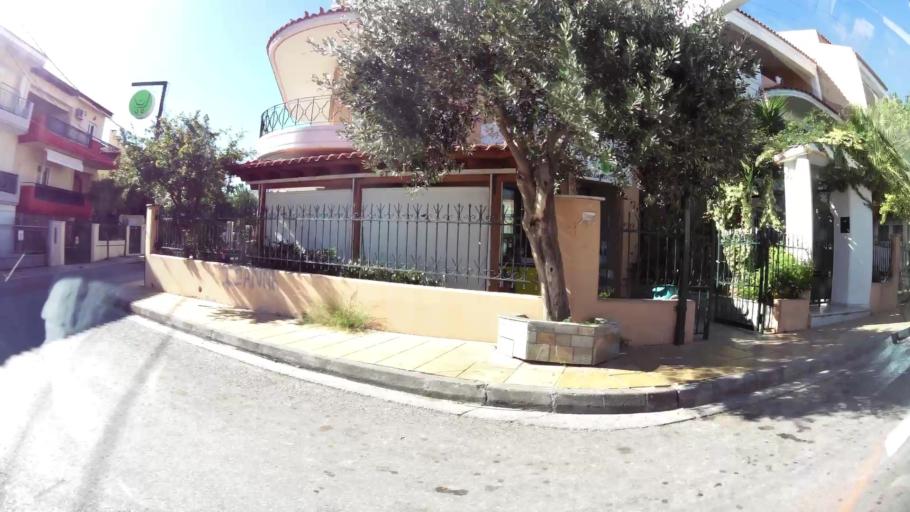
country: GR
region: Attica
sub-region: Nomarchia Anatolikis Attikis
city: Gerakas
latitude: 38.0069
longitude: 23.8521
